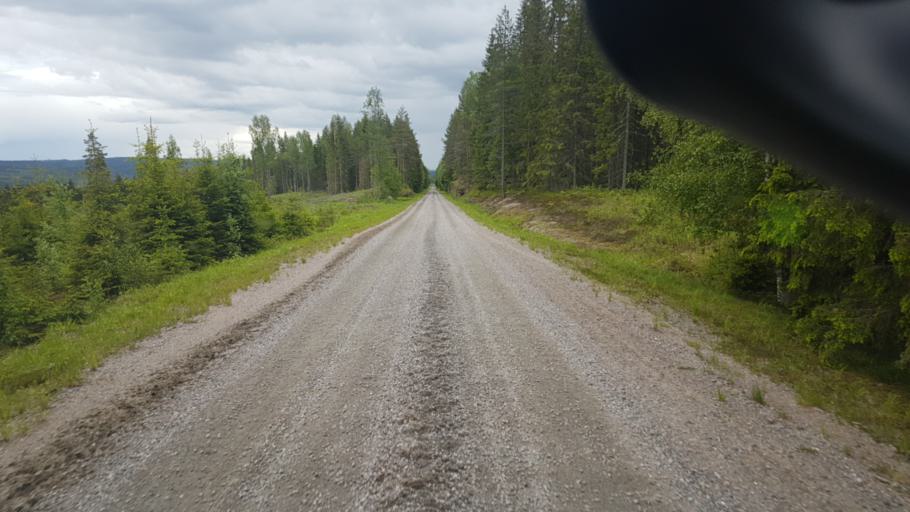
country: SE
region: Vaermland
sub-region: Eda Kommun
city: Charlottenberg
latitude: 60.0075
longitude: 12.5065
